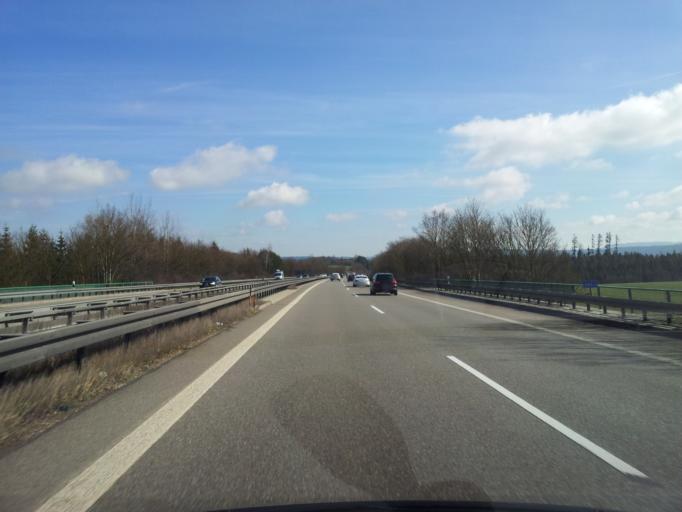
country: DE
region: Baden-Wuerttemberg
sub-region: Freiburg Region
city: Villingendorf
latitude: 48.1963
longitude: 8.5951
